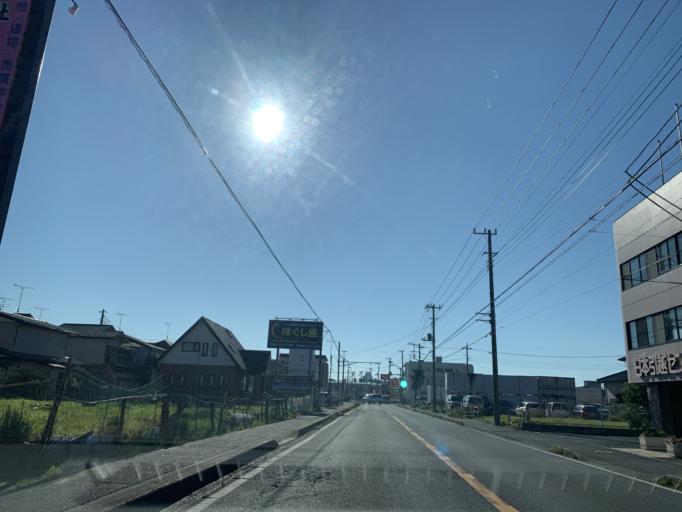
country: JP
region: Chiba
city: Matsudo
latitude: 35.7979
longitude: 139.8964
